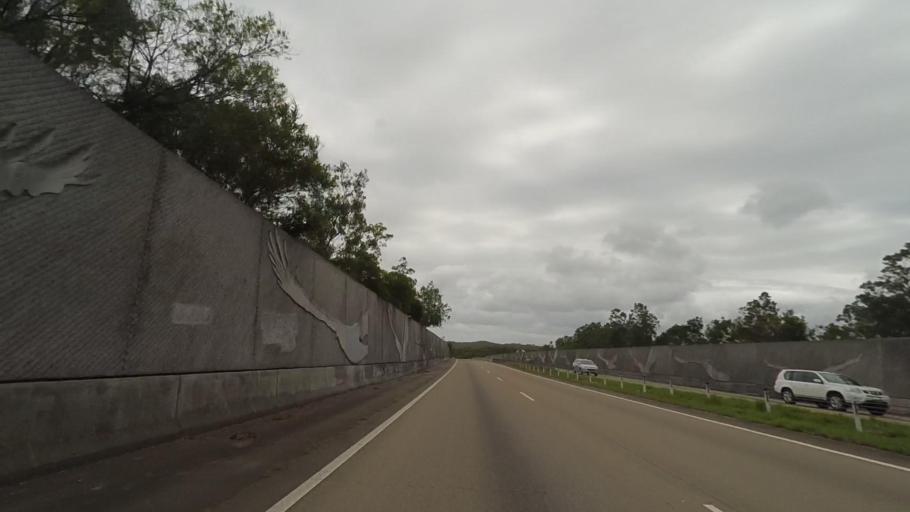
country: AU
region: New South Wales
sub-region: Lake Macquarie Shire
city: Kotara
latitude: -32.9572
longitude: 151.6798
